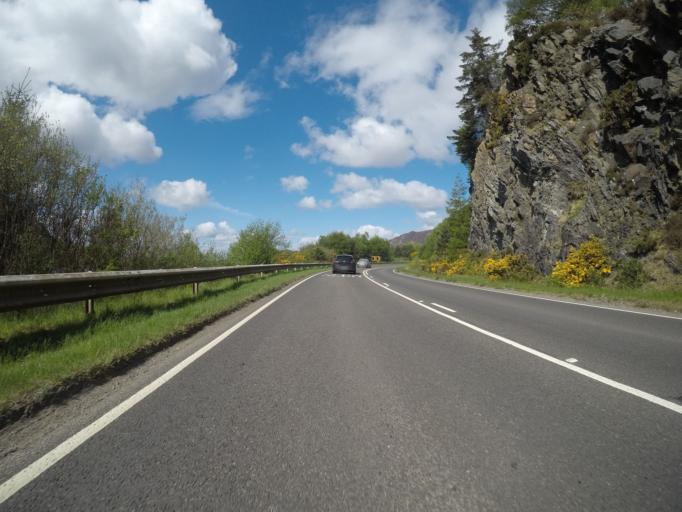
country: GB
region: Scotland
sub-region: Highland
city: Fort William
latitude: 57.2719
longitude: -5.5110
